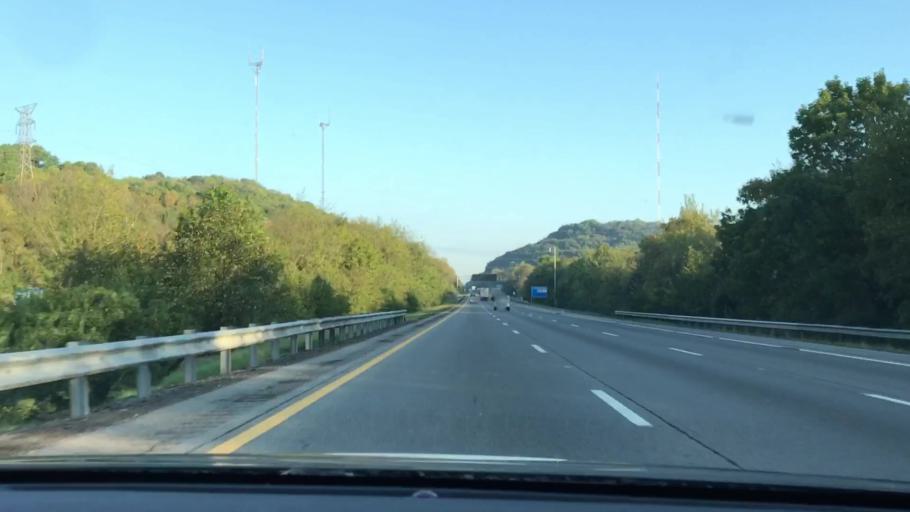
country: US
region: Tennessee
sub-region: Davidson County
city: Nashville
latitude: 36.2529
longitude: -86.7850
